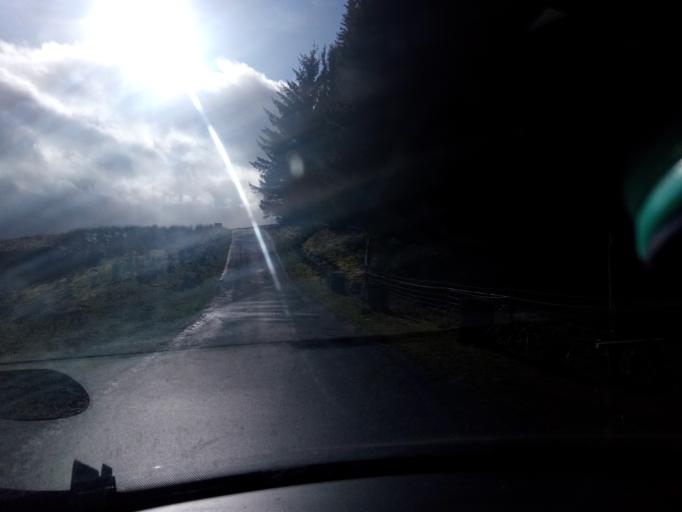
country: GB
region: England
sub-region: Northumberland
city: Rochester
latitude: 55.3282
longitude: -2.2928
